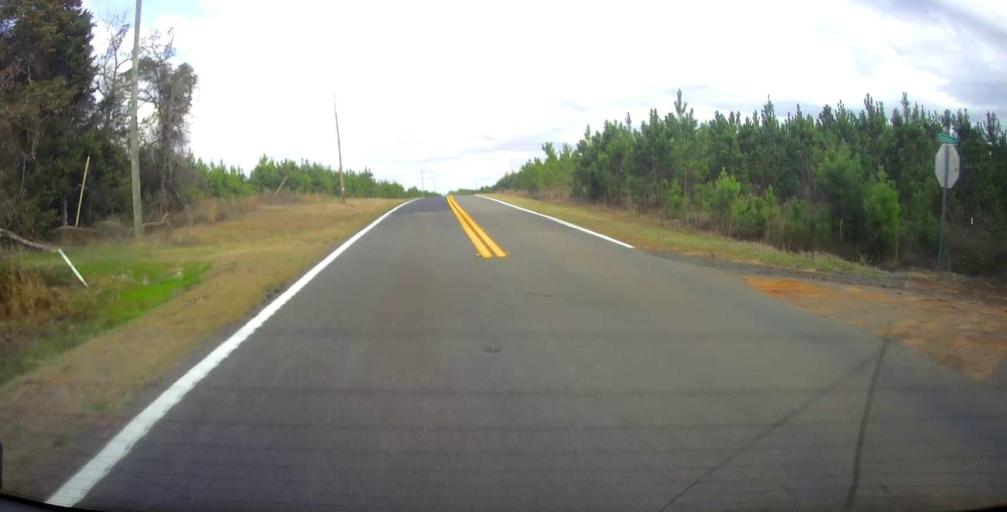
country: US
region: Georgia
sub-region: Marion County
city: Buena Vista
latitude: 32.4471
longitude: -84.4638
